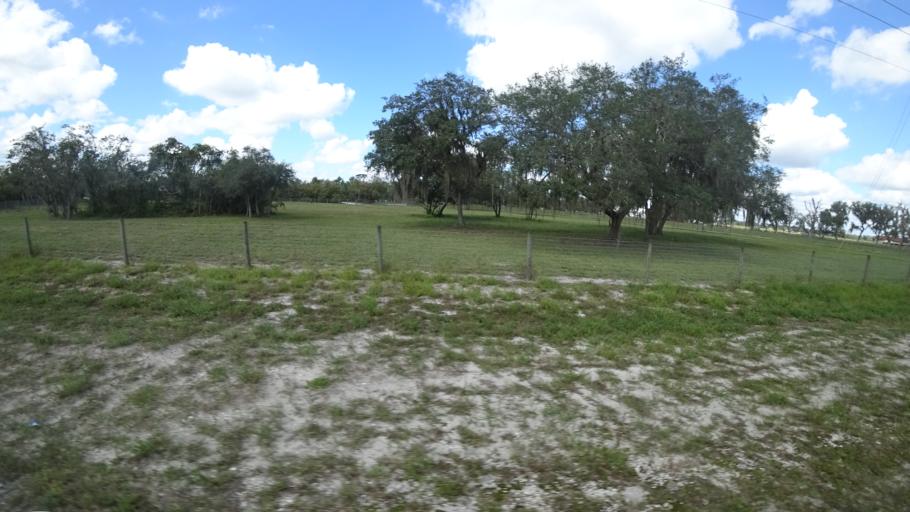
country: US
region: Florida
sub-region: Sarasota County
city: Lake Sarasota
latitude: 27.3597
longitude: -82.2277
